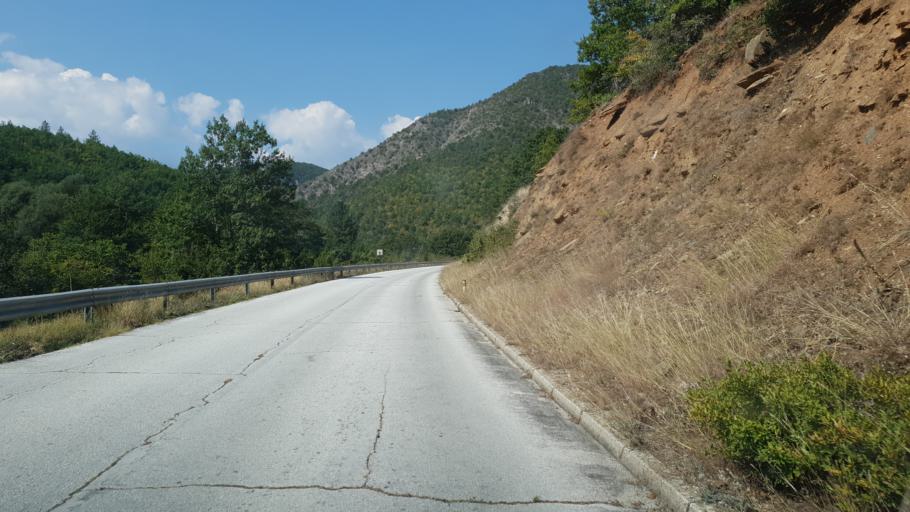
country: MK
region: Makedonski Brod
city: Samokov
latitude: 41.6686
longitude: 21.2459
